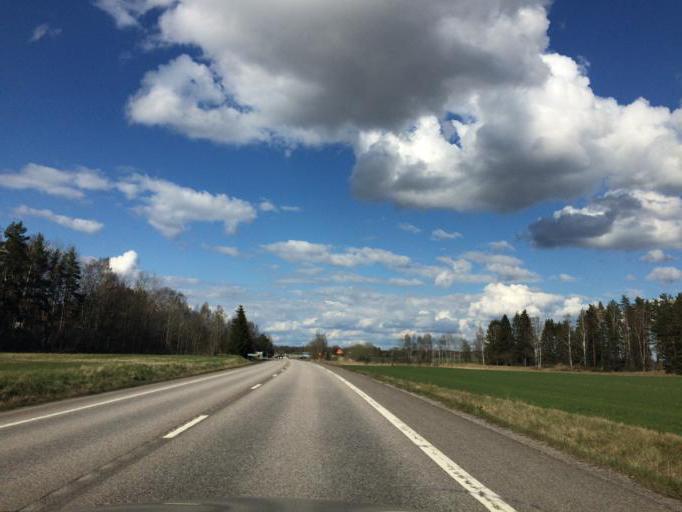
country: SE
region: Soedermanland
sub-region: Eskilstuna Kommun
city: Eskilstuna
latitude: 59.4094
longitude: 16.5804
